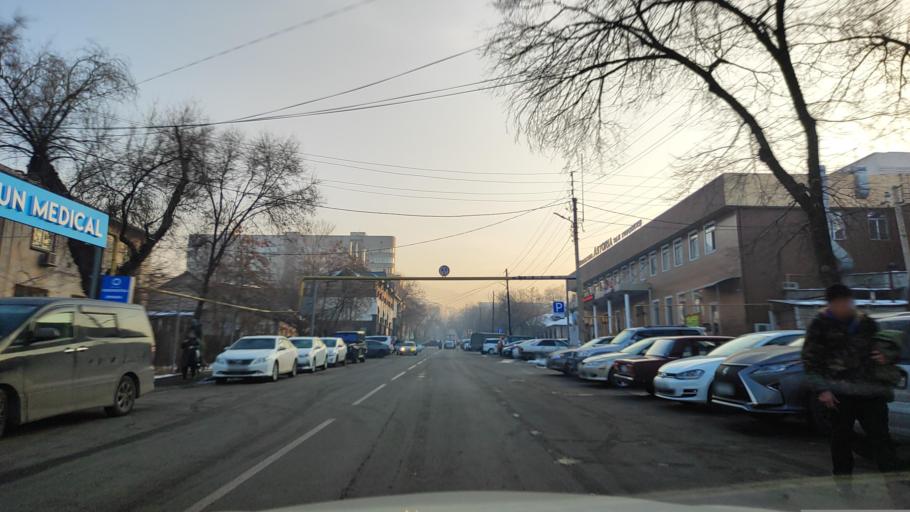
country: KZ
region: Almaty Qalasy
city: Almaty
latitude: 43.2573
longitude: 76.9601
